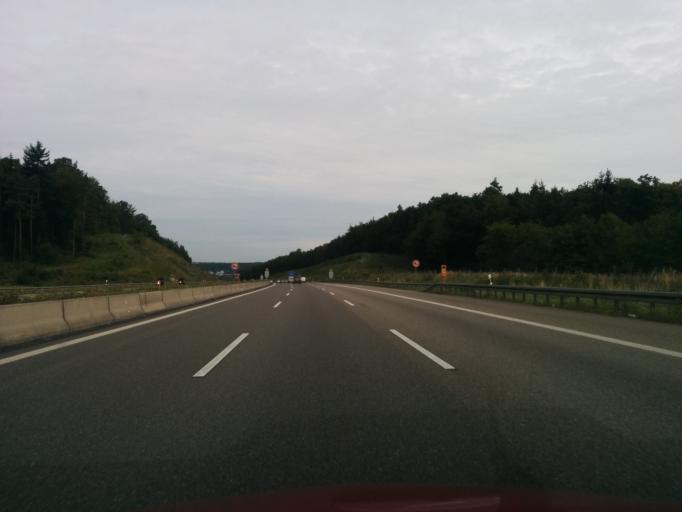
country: DE
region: Baden-Wuerttemberg
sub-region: Karlsruhe Region
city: Niefern-Oschelbronn
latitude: 48.8945
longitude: 8.7852
